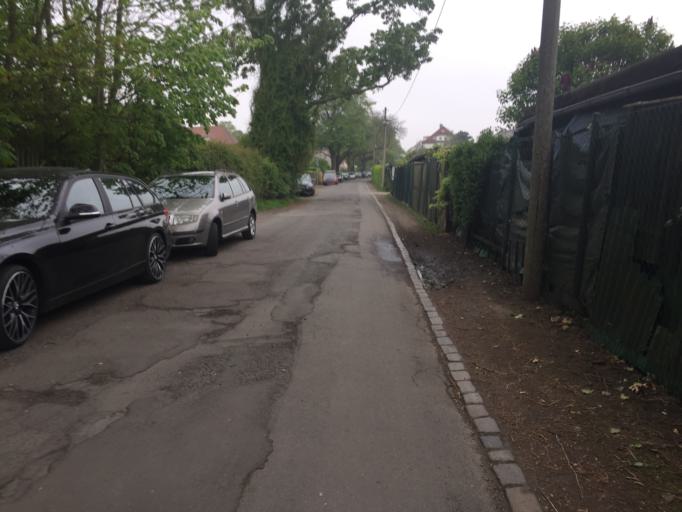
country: DE
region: Saxony
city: Leipzig
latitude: 51.3360
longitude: 12.4259
